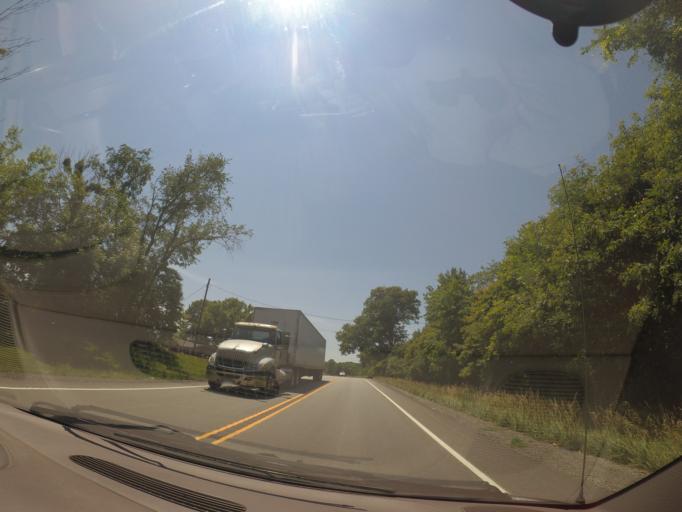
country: US
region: Indiana
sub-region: LaPorte County
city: Westville
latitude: 41.6084
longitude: -86.8954
